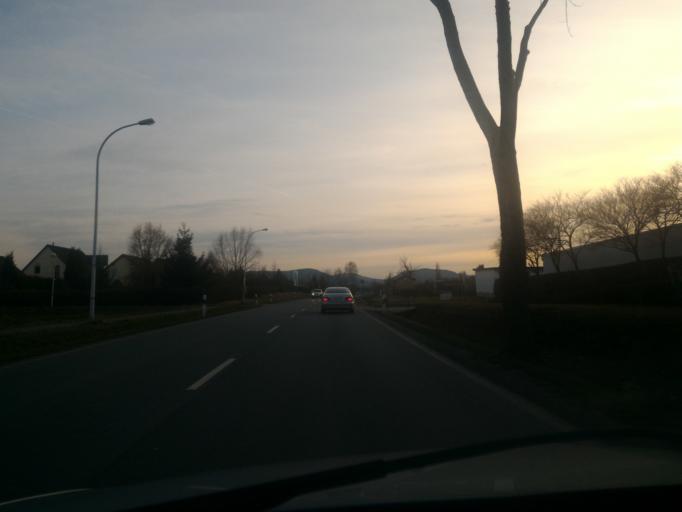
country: DE
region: Saxony
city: Zittau
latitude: 50.8904
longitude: 14.7949
